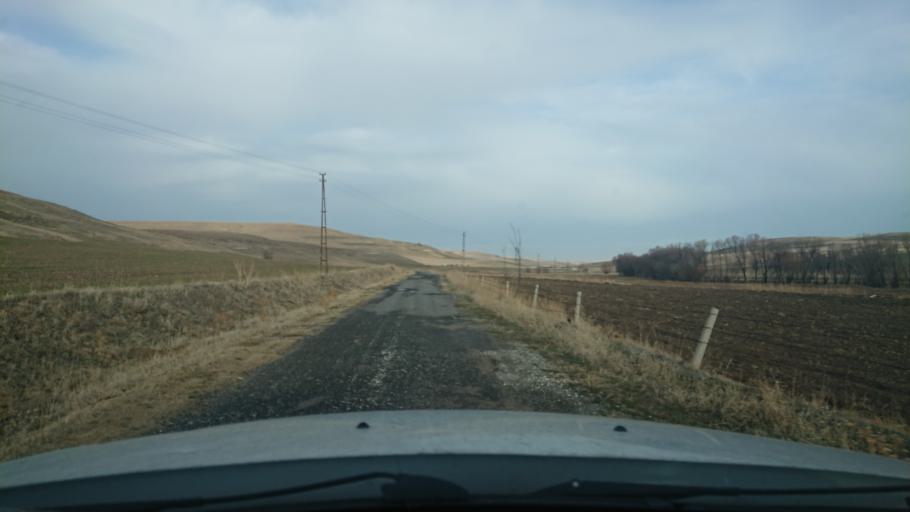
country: TR
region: Aksaray
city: Acipinar
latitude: 38.6787
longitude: 33.8663
